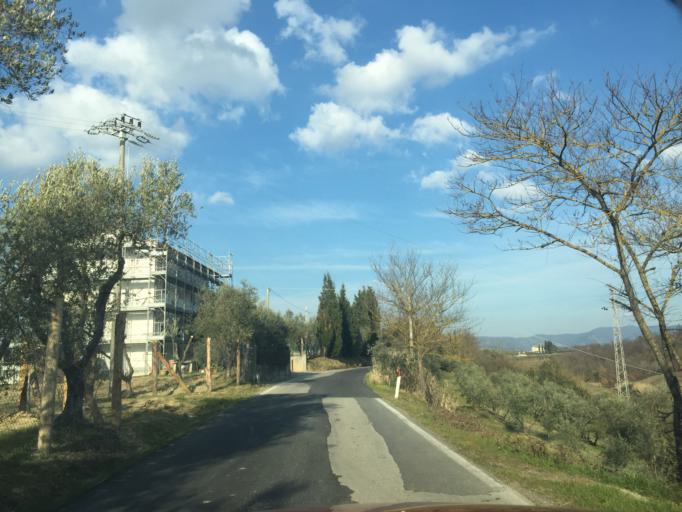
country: IT
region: Tuscany
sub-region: Province of Florence
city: Stabbia
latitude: 43.7599
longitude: 10.8351
